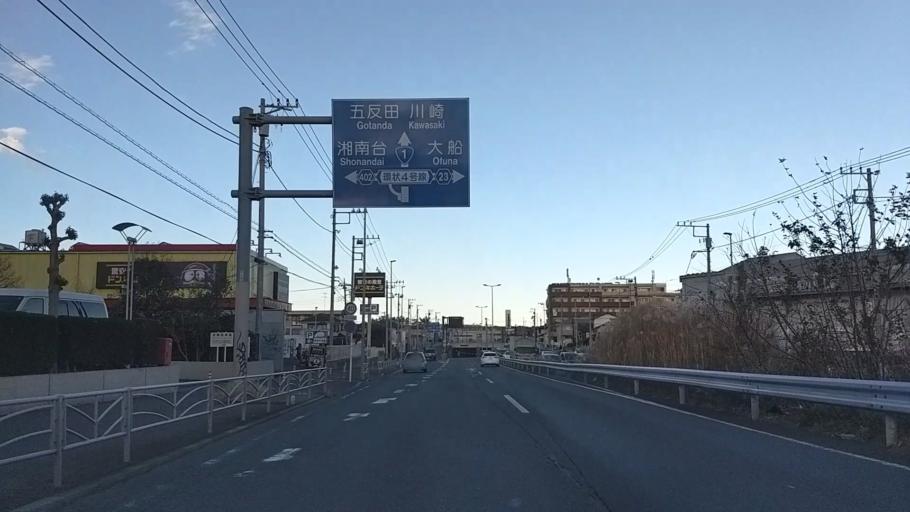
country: JP
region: Kanagawa
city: Fujisawa
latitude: 35.3745
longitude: 139.5034
